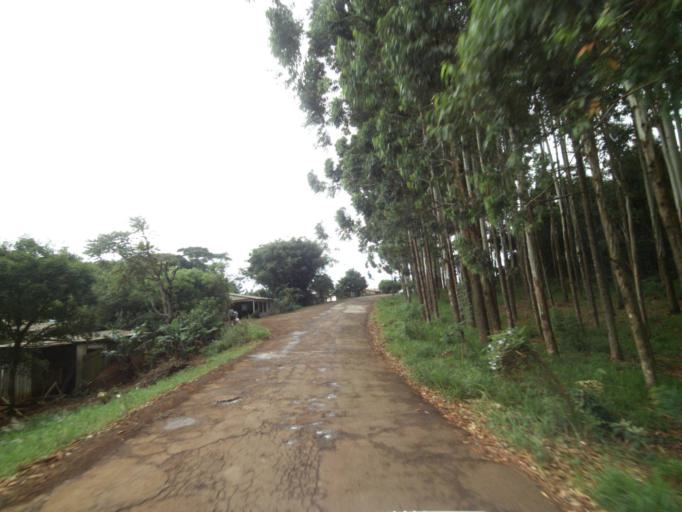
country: BR
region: Parana
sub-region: Guaraniacu
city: Guaraniacu
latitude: -25.1193
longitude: -52.8502
